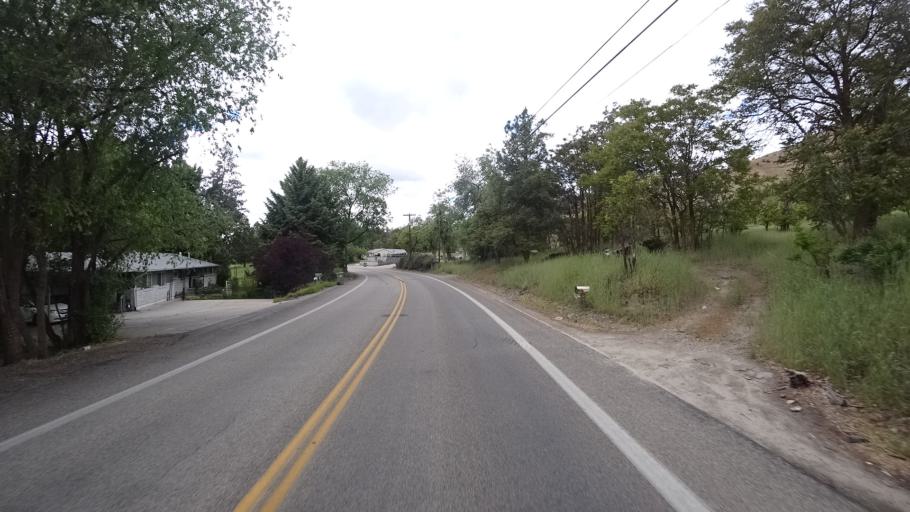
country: US
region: Idaho
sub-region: Ada County
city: Garden City
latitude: 43.6724
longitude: -116.2563
